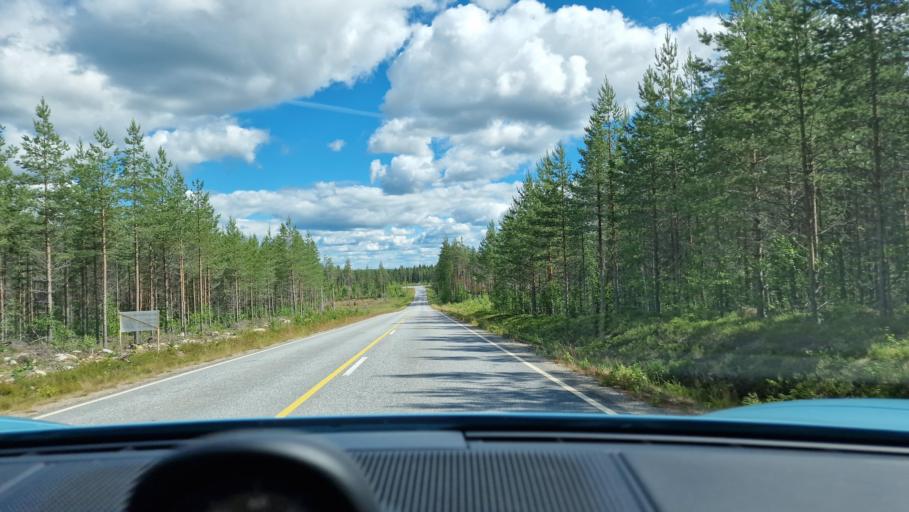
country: FI
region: Central Finland
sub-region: Saarijaervi-Viitasaari
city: Pylkoenmaeki
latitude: 62.6605
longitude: 24.5627
